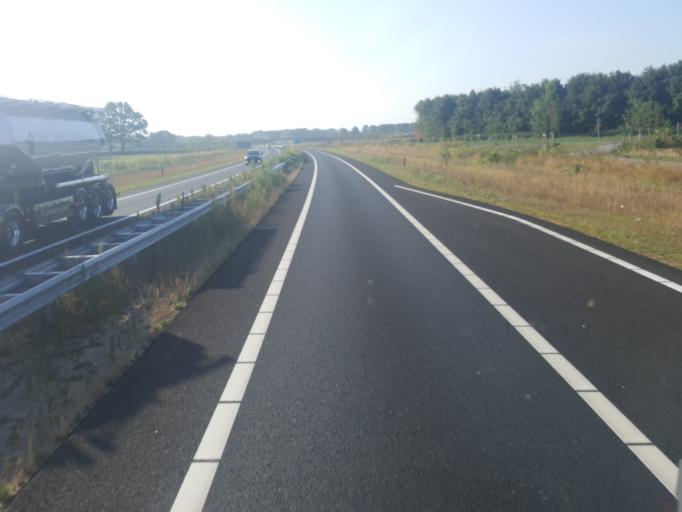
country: NL
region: Gelderland
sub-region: Berkelland
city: Eibergen
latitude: 52.0926
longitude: 6.6243
